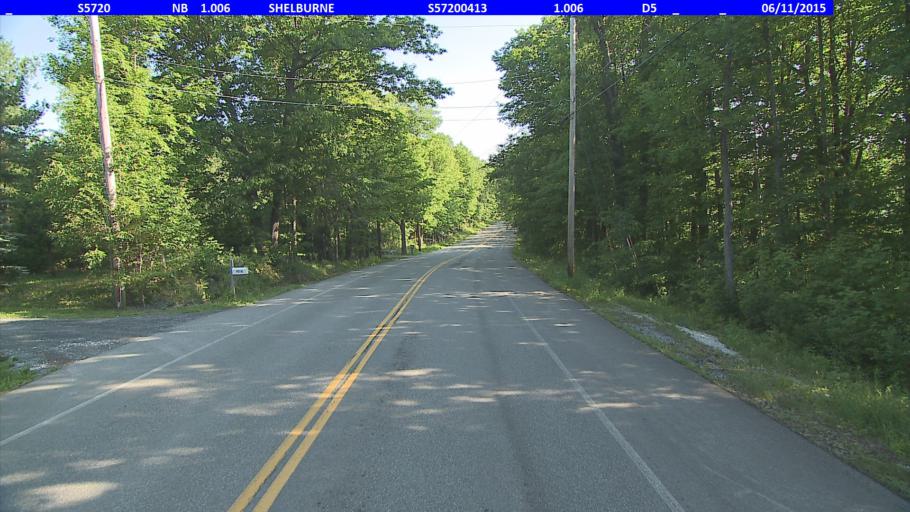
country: US
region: Vermont
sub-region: Chittenden County
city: South Burlington
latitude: 44.3825
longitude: -73.2019
